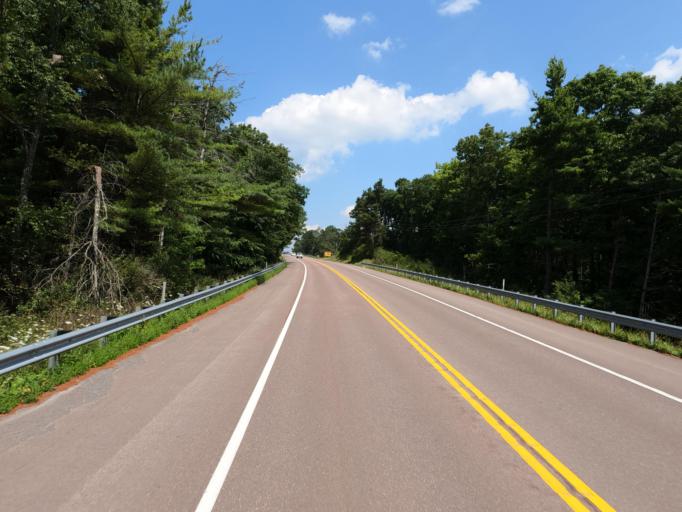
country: US
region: Maryland
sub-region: Garrett County
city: Mountain Lake Park
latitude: 39.4562
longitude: -79.3706
